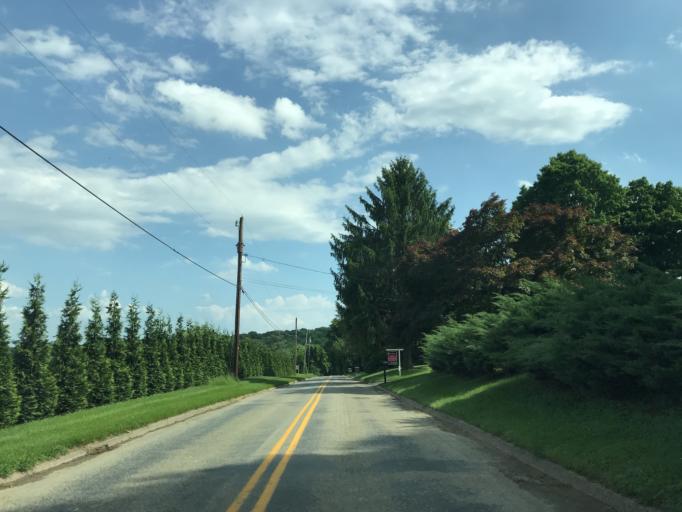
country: US
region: Pennsylvania
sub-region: York County
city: Susquehanna Trails
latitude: 39.6578
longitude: -76.3784
